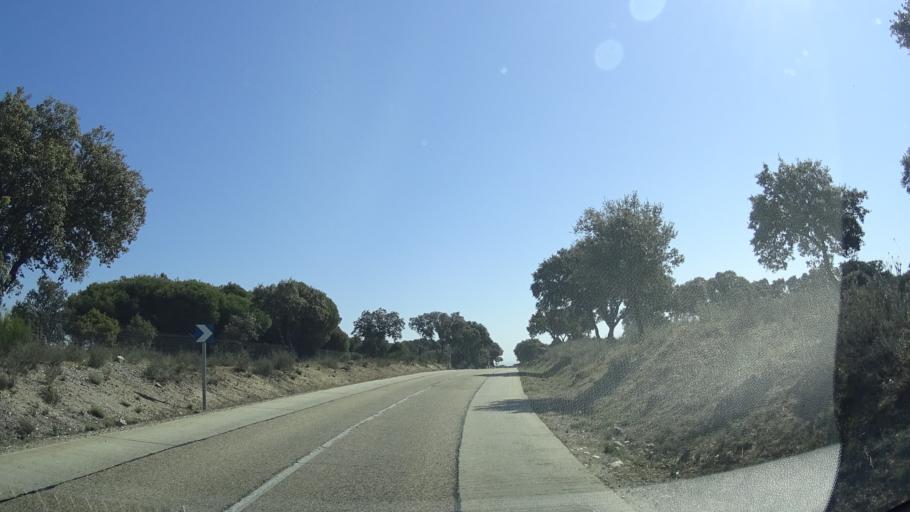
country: ES
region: Madrid
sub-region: Provincia de Madrid
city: Hoyo de Manzanares
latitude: 40.6449
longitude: -3.8399
